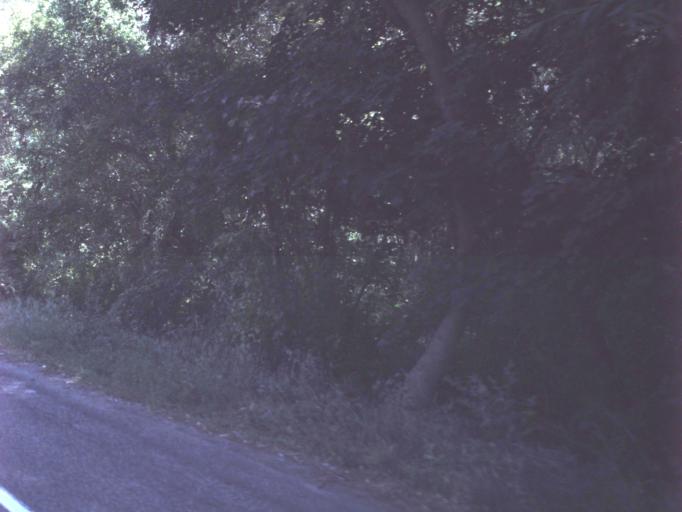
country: US
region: Utah
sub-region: Cache County
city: North Logan
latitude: 41.7630
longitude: -111.6983
